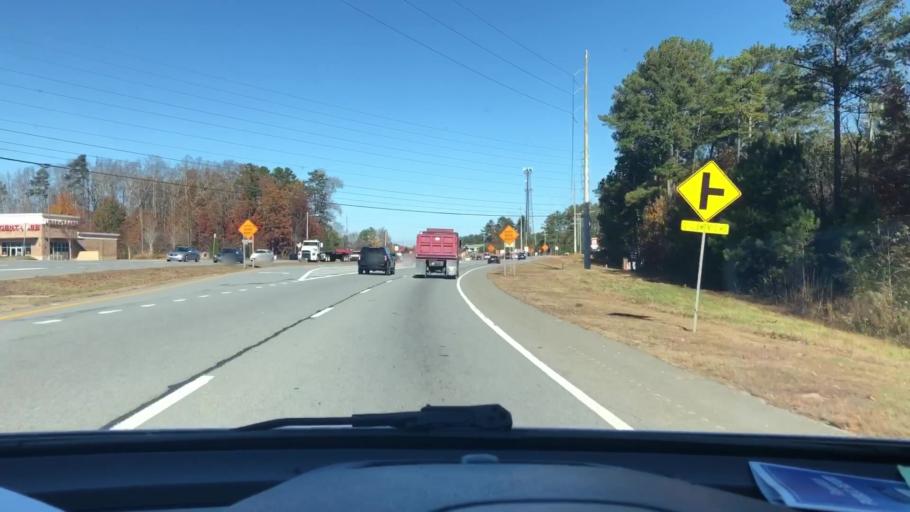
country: US
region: Georgia
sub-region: Fulton County
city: Johns Creek
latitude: 34.1173
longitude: -84.1754
